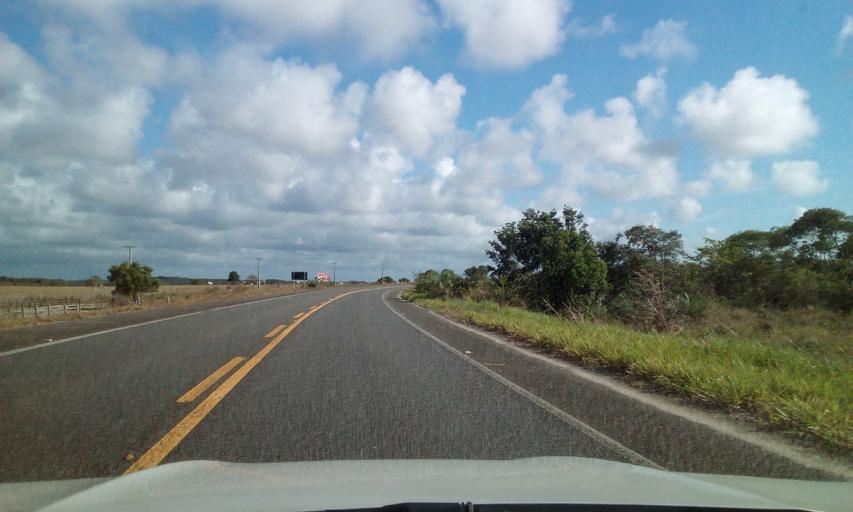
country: BR
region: Bahia
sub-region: Conde
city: Conde
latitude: -11.7498
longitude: -37.5861
